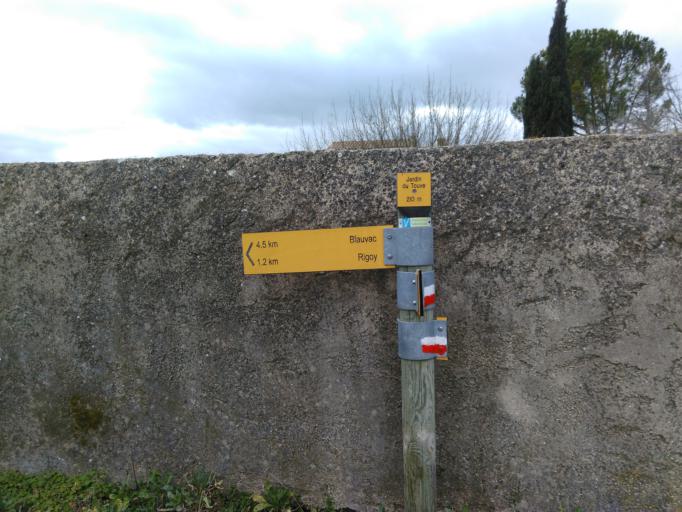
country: FR
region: Provence-Alpes-Cote d'Azur
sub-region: Departement du Vaucluse
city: Malemort-du-Comtat
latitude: 44.0215
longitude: 5.1623
